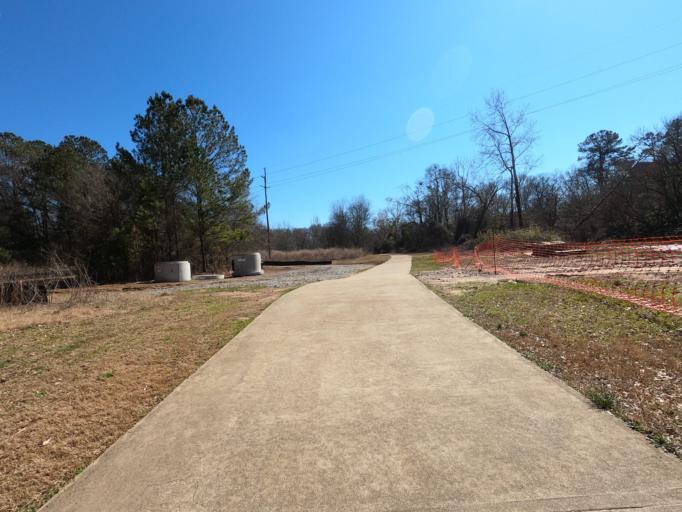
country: US
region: Georgia
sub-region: Clarke County
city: Athens
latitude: 33.9741
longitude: -83.3813
